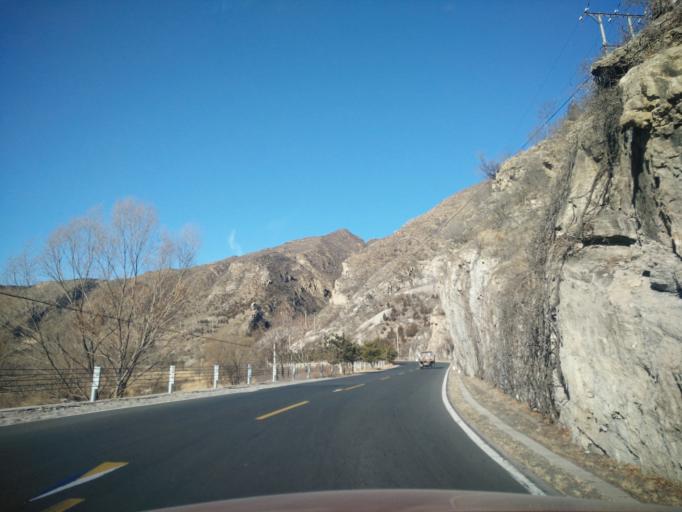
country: CN
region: Beijing
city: Yanchi
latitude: 40.0336
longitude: 115.8498
